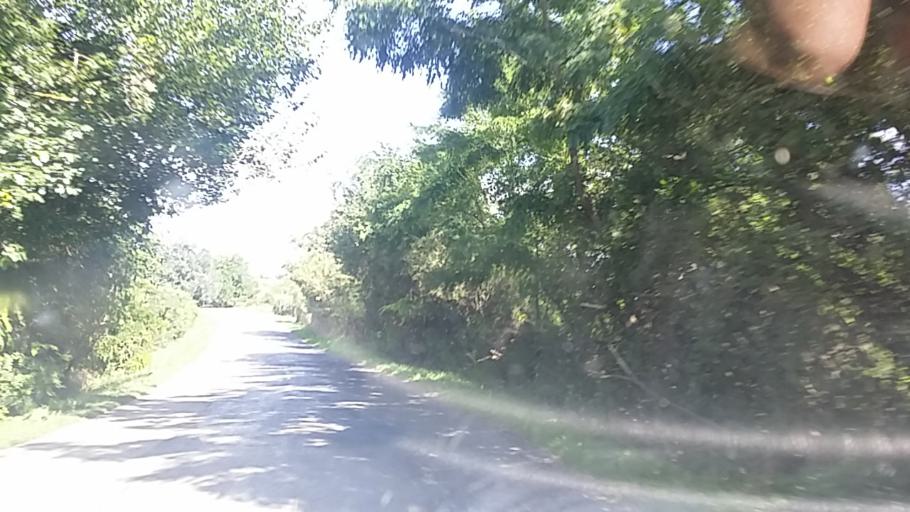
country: HU
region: Tolna
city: Hogyesz
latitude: 46.5209
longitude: 18.4145
